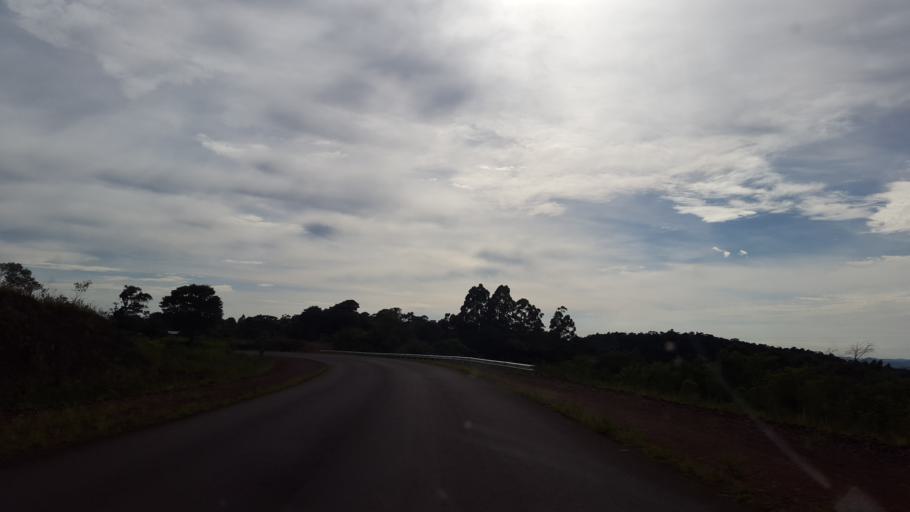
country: AR
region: Misiones
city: Bernardo de Irigoyen
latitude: -26.4203
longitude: -53.8280
